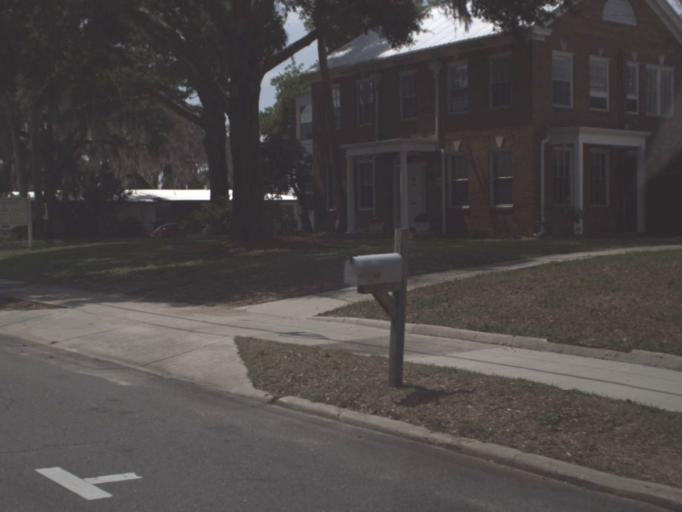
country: US
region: Florida
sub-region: Lake County
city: Eustis
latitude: 28.8609
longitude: -81.6859
